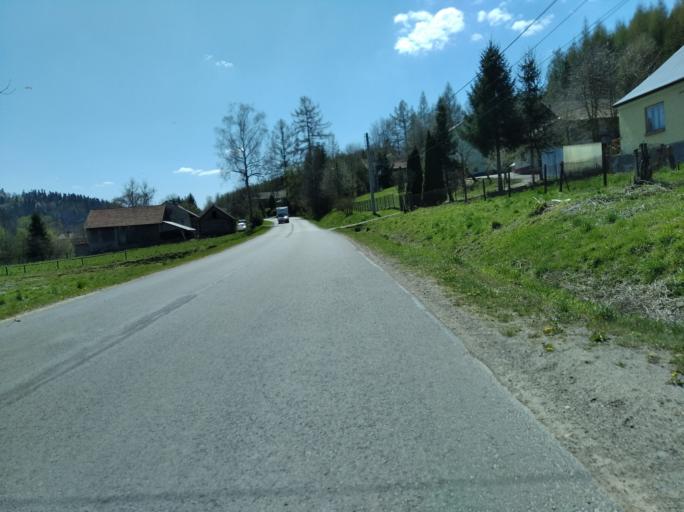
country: PL
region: Subcarpathian Voivodeship
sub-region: Powiat brzozowski
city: Dydnia
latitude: 49.6923
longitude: 22.1838
